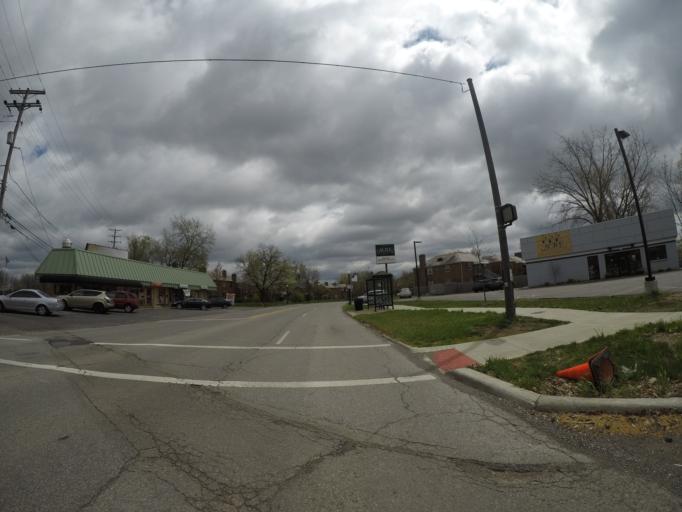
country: US
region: Ohio
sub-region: Franklin County
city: Grandview Heights
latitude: 39.9936
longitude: -83.0422
